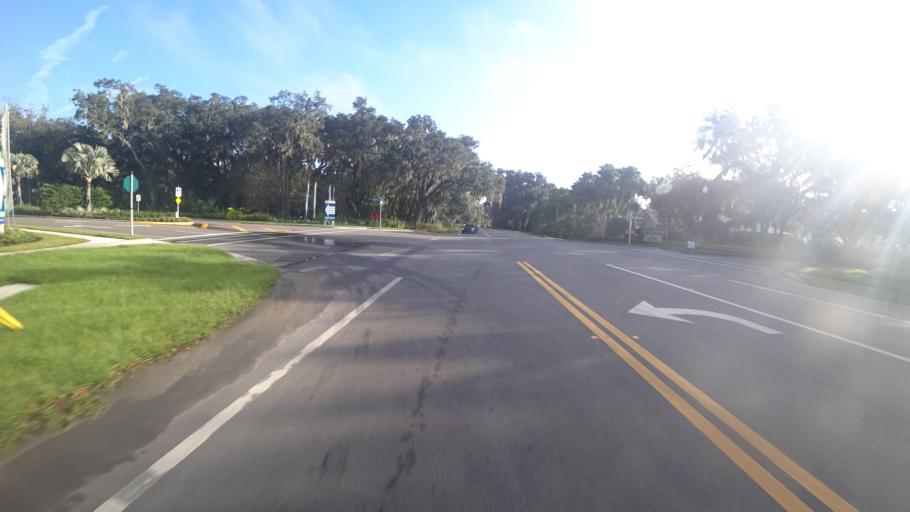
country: US
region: Florida
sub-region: Manatee County
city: Ellenton
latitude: 27.5448
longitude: -82.4520
